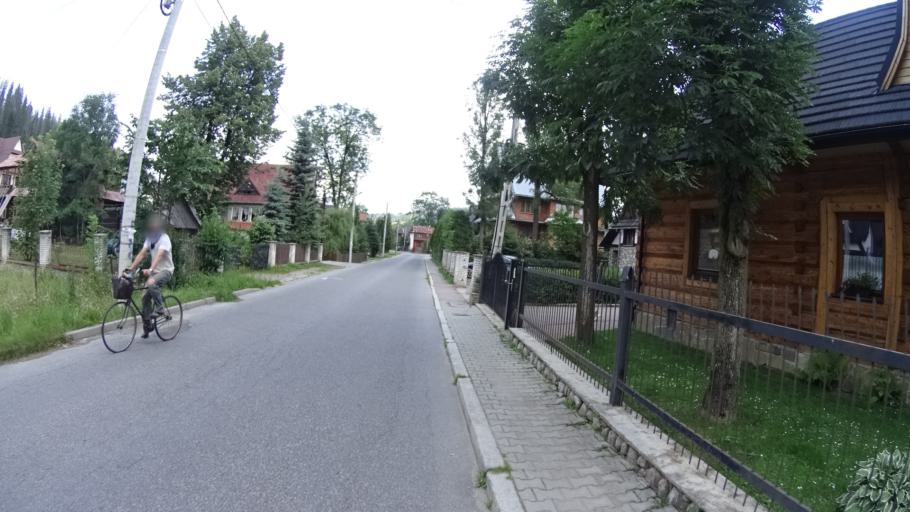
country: PL
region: Lesser Poland Voivodeship
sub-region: Powiat tatrzanski
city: Poronin
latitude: 49.3307
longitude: 19.9965
